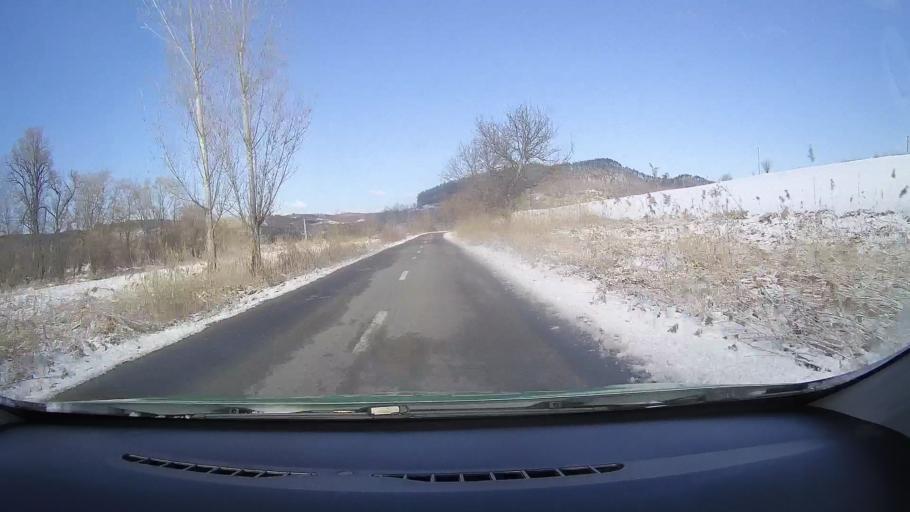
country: RO
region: Sibiu
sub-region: Comuna Mihaileni
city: Mihaileni
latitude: 46.0034
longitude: 24.3620
